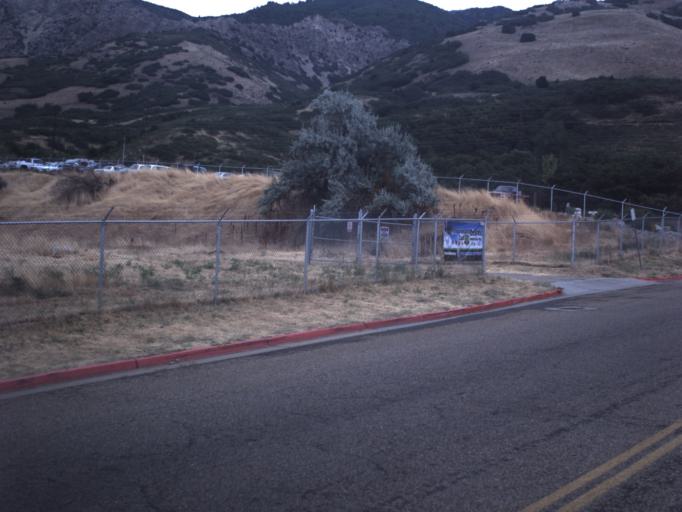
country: US
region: Utah
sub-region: Weber County
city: South Ogden
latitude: 41.1948
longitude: -111.9390
